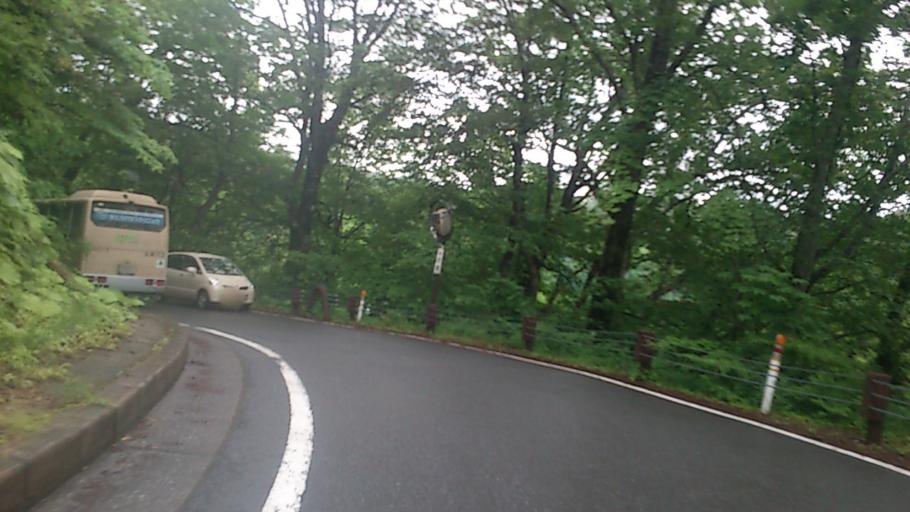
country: JP
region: Akita
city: Noshiromachi
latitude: 40.5648
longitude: 139.9710
